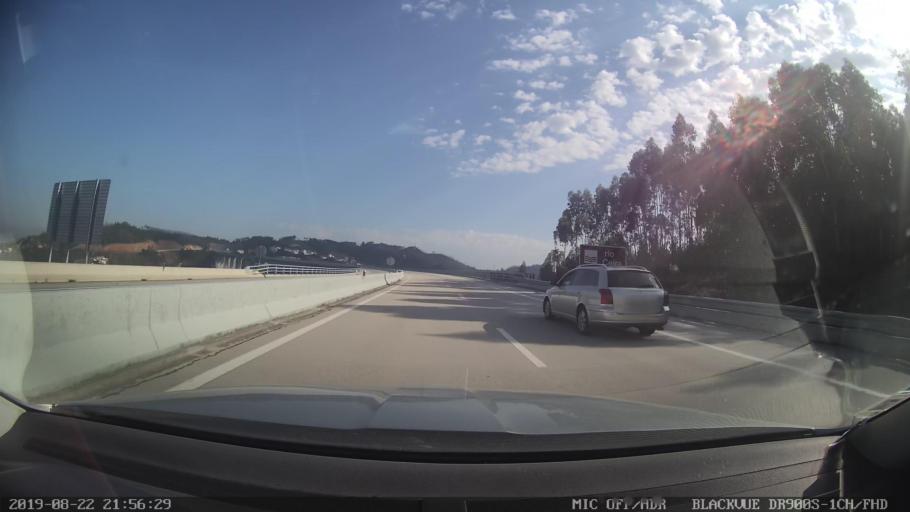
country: PT
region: Coimbra
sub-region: Coimbra
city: Coimbra
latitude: 40.1710
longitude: -8.3777
